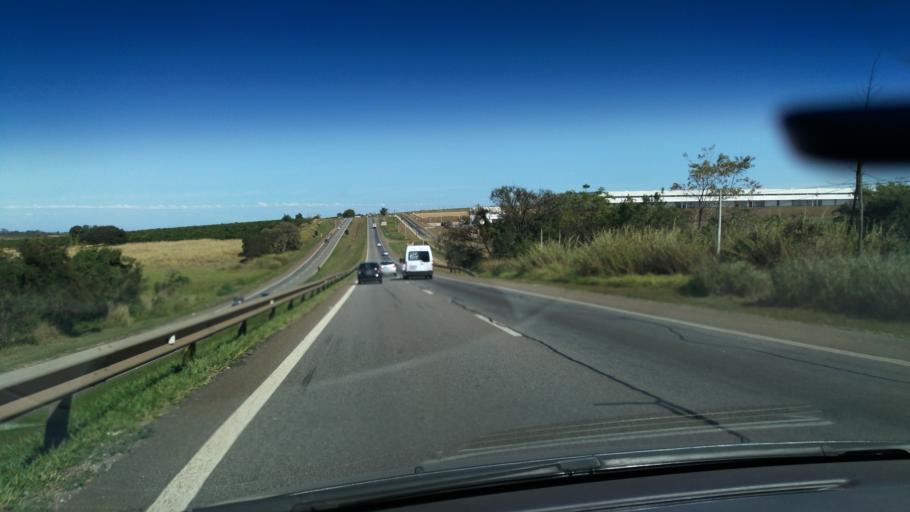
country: BR
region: Sao Paulo
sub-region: Santo Antonio De Posse
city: Santo Antonio de Posse
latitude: -22.5387
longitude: -46.9964
